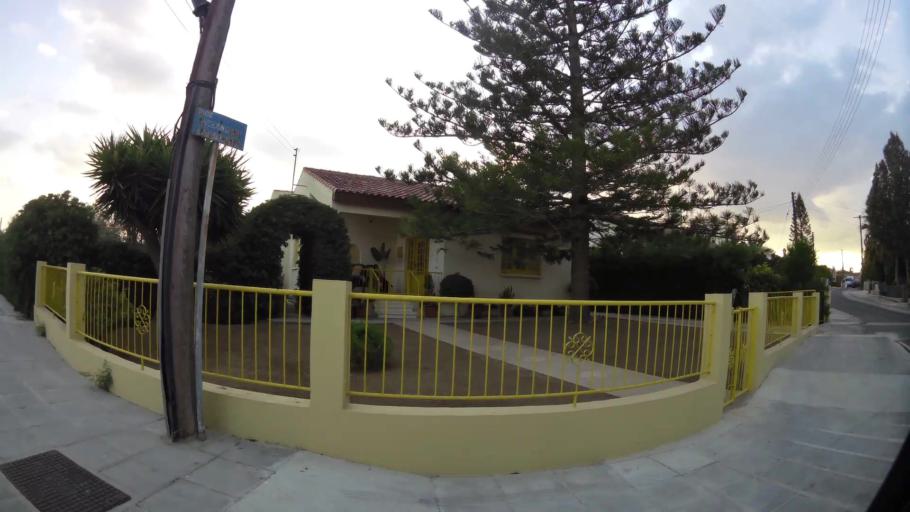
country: CY
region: Larnaka
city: Meneou
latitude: 34.8661
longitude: 33.5909
